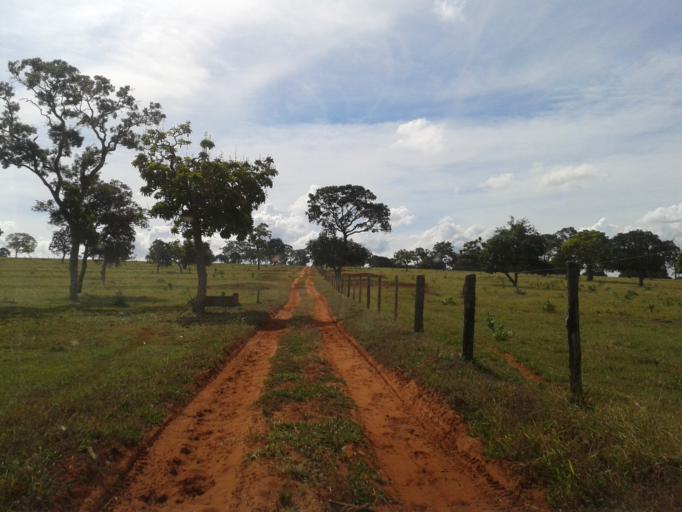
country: BR
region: Minas Gerais
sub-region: Campina Verde
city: Campina Verde
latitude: -19.4439
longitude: -49.6302
